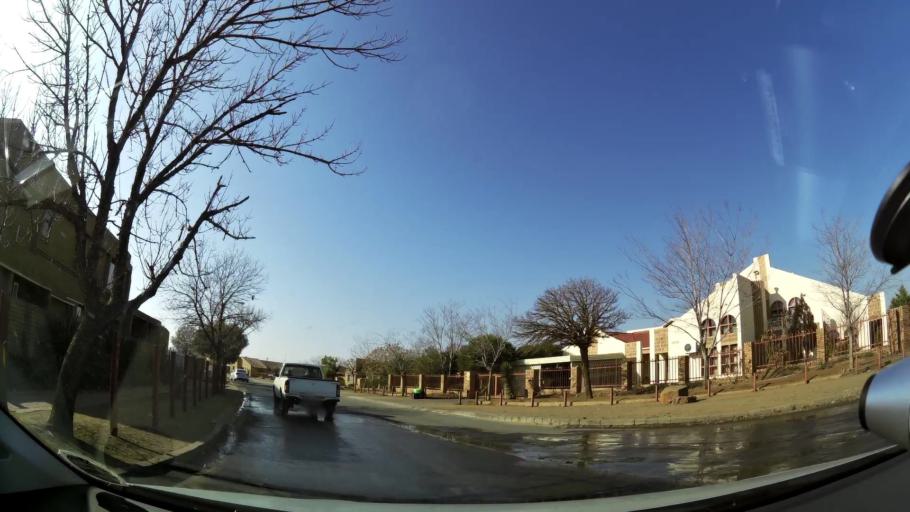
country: ZA
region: Orange Free State
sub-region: Mangaung Metropolitan Municipality
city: Bloemfontein
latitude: -29.1898
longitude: 26.2215
